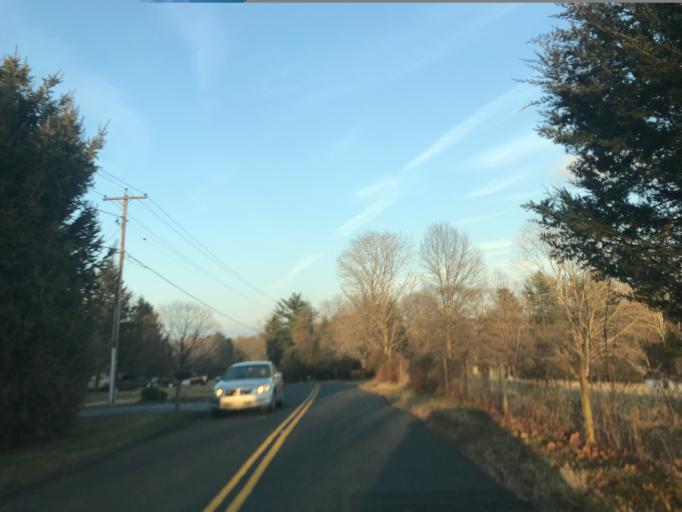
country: US
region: Maryland
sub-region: Harford County
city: Riverside
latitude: 39.4925
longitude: -76.2672
